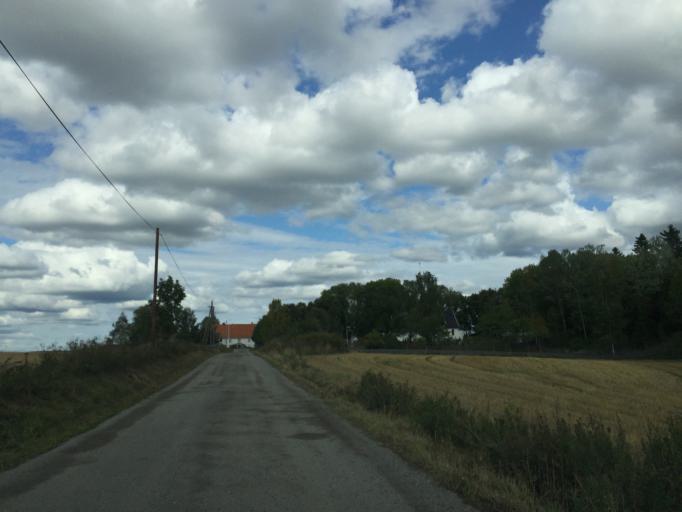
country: NO
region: Ostfold
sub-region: Hobol
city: Elvestad
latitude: 59.5990
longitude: 10.9218
